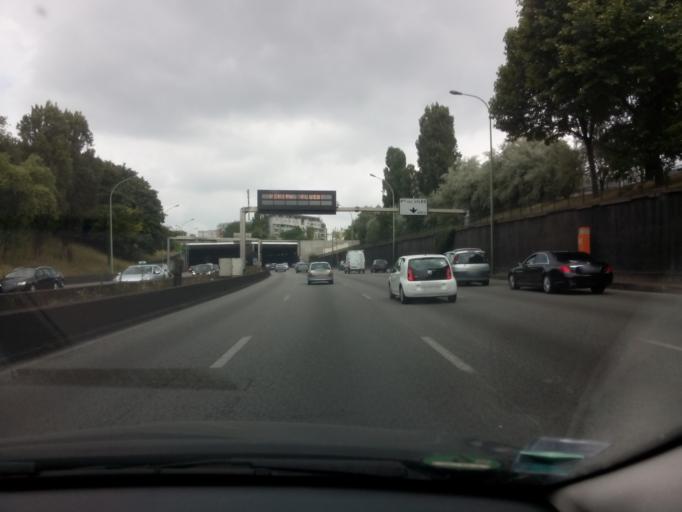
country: FR
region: Ile-de-France
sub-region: Departement de Seine-Saint-Denis
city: Bagnolet
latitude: 48.8702
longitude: 2.4133
